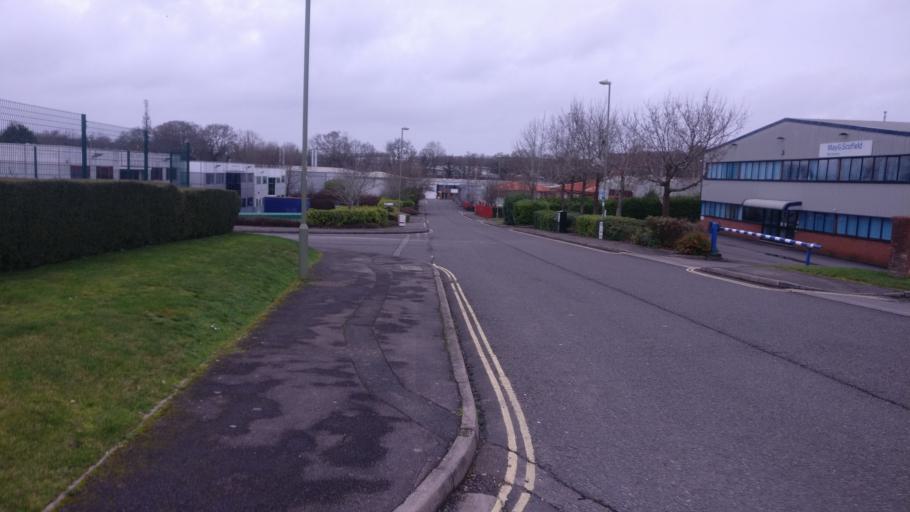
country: GB
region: England
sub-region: Hampshire
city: Basingstoke
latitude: 51.2763
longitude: -1.0643
